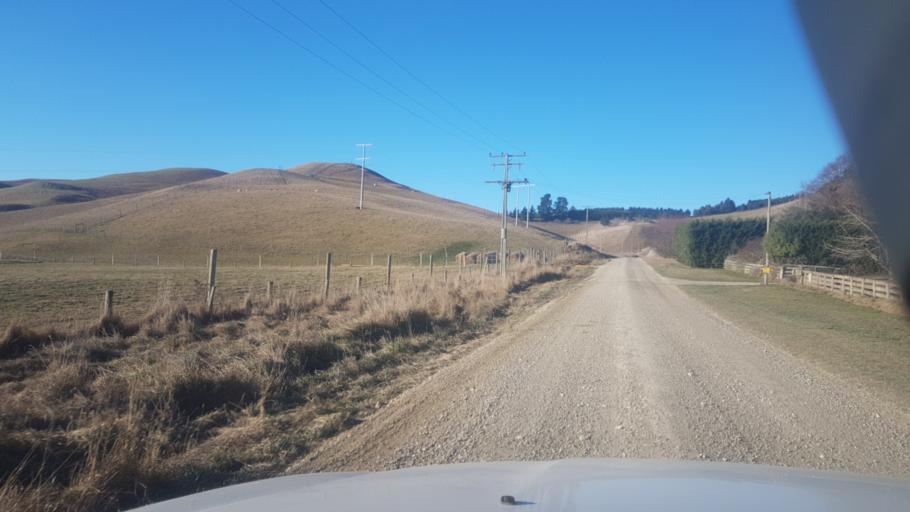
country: NZ
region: Canterbury
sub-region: Timaru District
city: Pleasant Point
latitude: -44.3433
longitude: 171.0598
